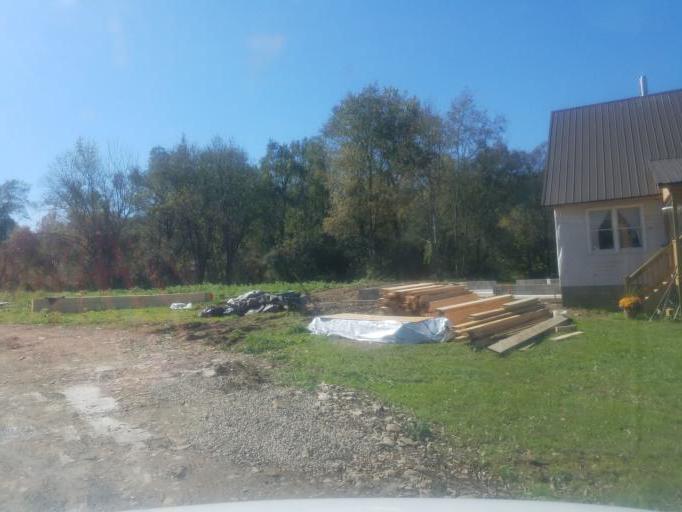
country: US
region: New York
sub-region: Allegany County
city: Friendship
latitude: 42.3063
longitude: -78.1100
